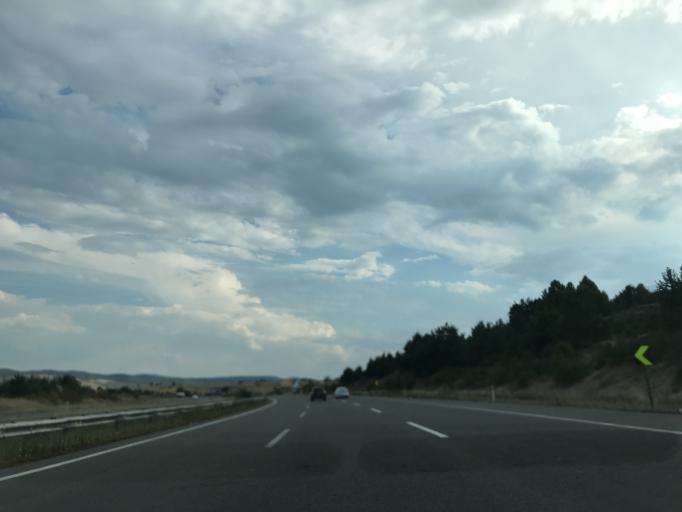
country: TR
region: Bolu
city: Gerede
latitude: 40.6856
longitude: 32.2215
